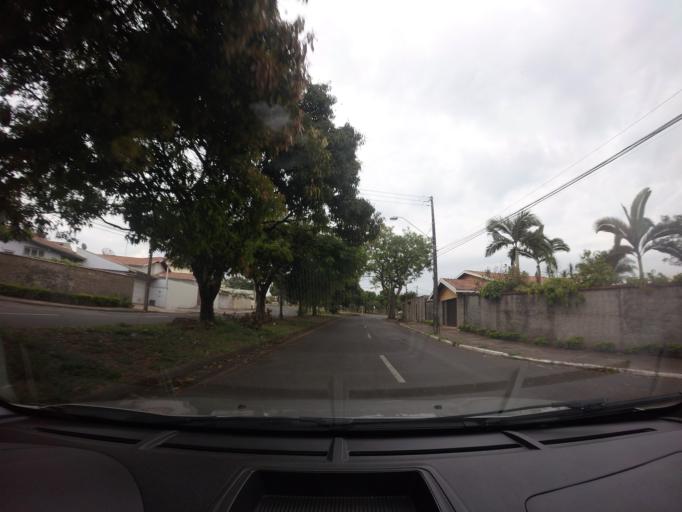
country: BR
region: Sao Paulo
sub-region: Piracicaba
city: Piracicaba
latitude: -22.7647
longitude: -47.5914
